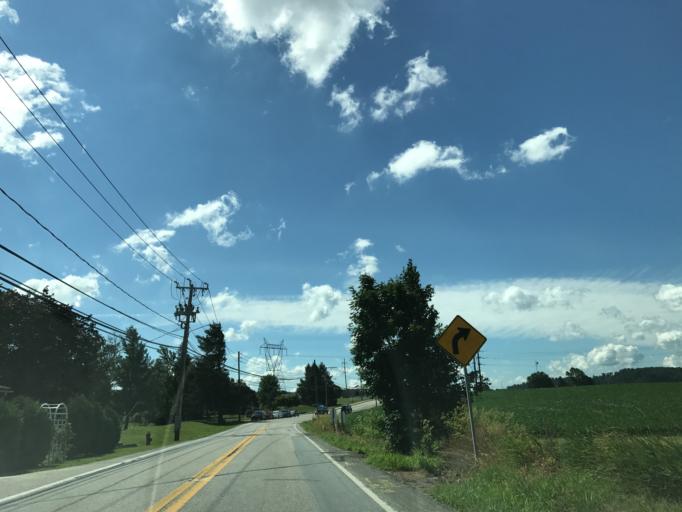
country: US
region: Pennsylvania
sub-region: Lancaster County
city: Maytown
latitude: 40.0706
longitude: -76.5778
